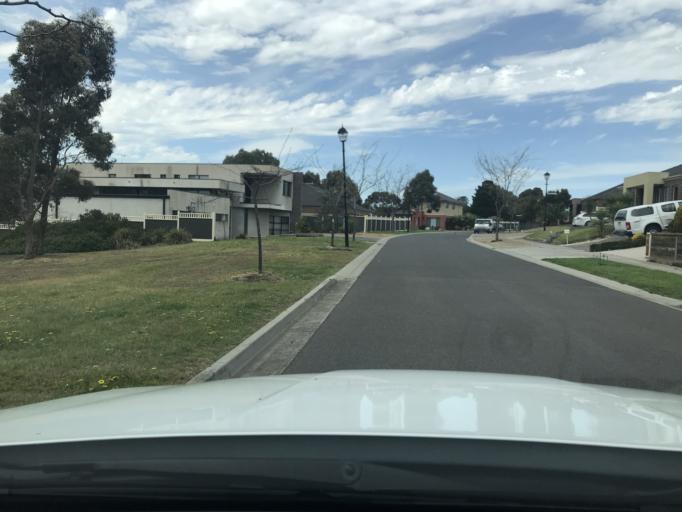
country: AU
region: Victoria
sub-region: Hume
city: Roxburgh Park
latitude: -37.6006
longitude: 144.9147
